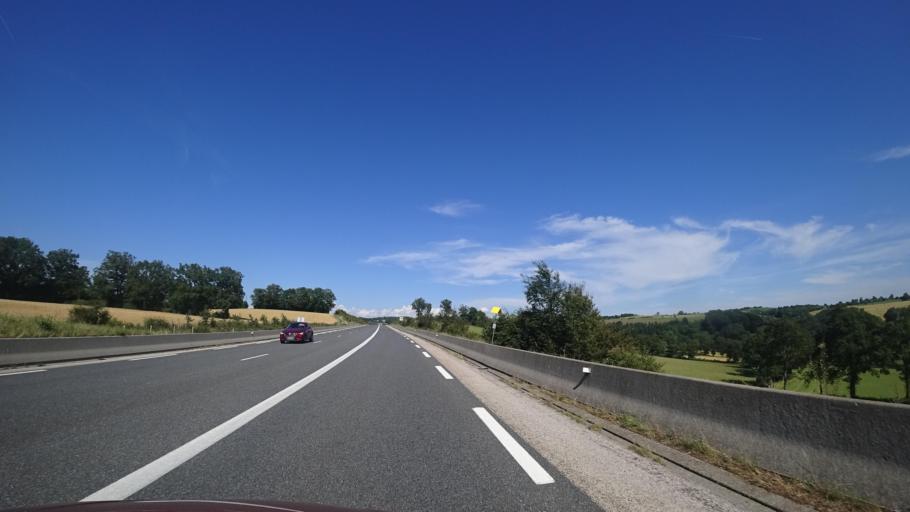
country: FR
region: Midi-Pyrenees
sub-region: Departement de l'Aveyron
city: Pont-de-Salars
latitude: 44.2719
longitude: 2.7344
